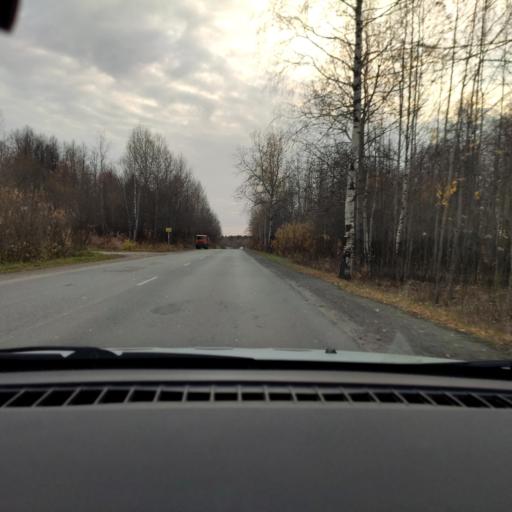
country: RU
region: Perm
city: Perm
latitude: 58.0985
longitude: 56.4077
